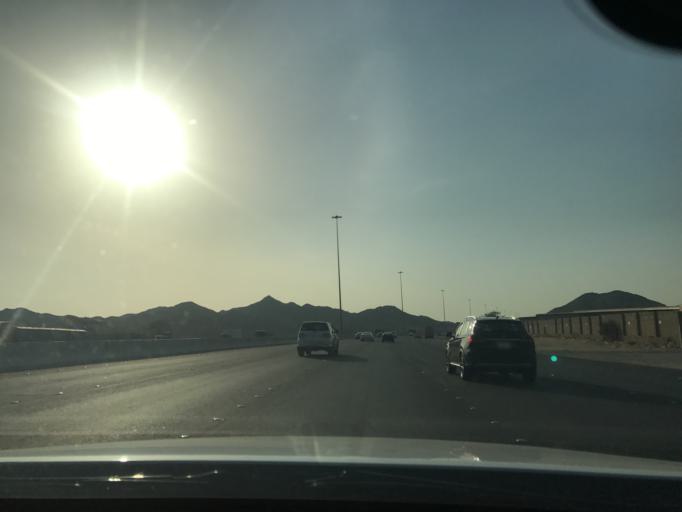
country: SA
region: Makkah
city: Jeddah
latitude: 21.3909
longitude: 39.4153
